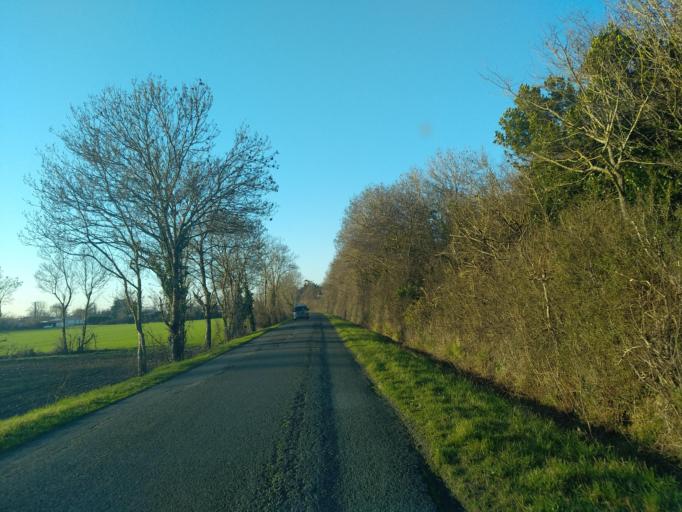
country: FR
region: Pays de la Loire
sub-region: Departement de la Vendee
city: Triaize
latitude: 46.3954
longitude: -1.2977
